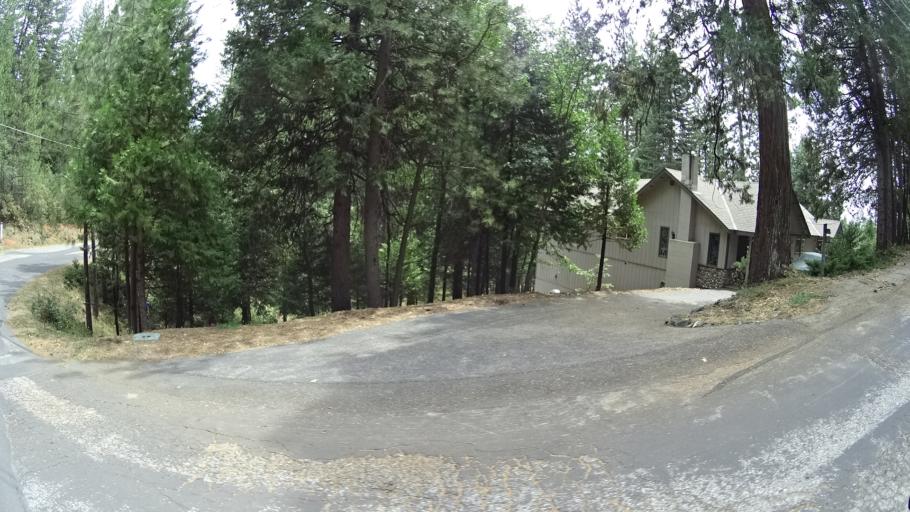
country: US
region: California
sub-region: Calaveras County
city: Arnold
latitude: 38.2361
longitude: -120.3503
